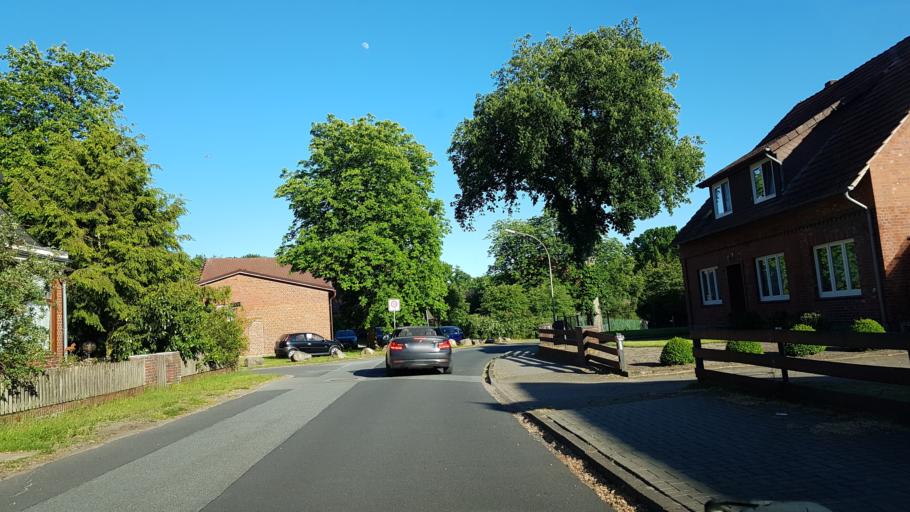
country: DE
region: Lower Saxony
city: Brackel
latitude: 53.3127
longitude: 10.0762
